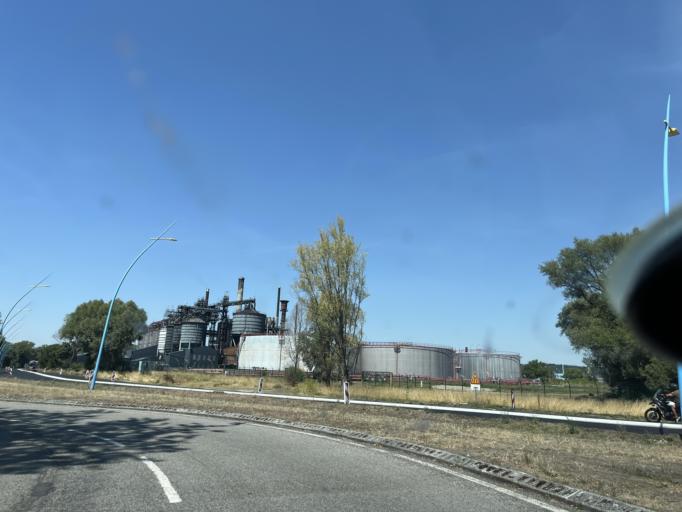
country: FR
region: Haute-Normandie
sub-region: Departement de l'Eure
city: Quillebeuf-sur-Seine
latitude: 49.4738
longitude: 0.5358
